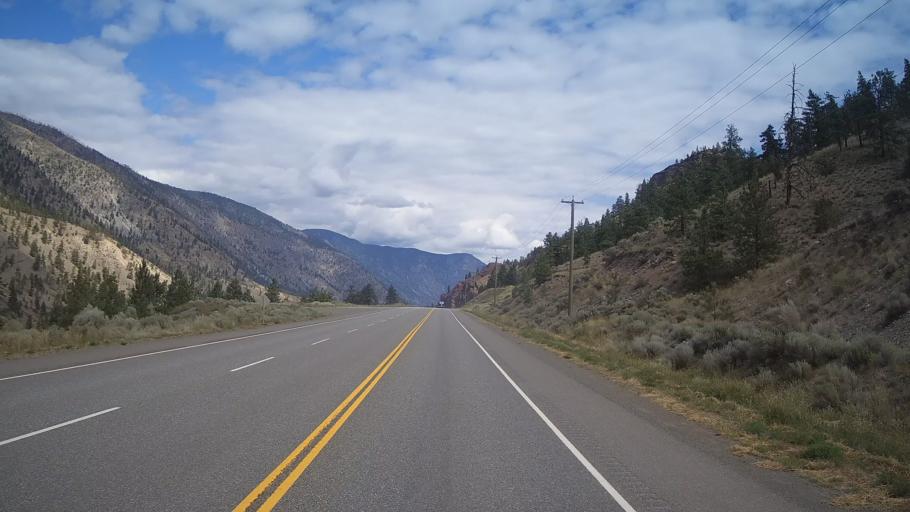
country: CA
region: British Columbia
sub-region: Thompson-Nicola Regional District
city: Ashcroft
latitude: 50.2964
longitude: -121.3924
